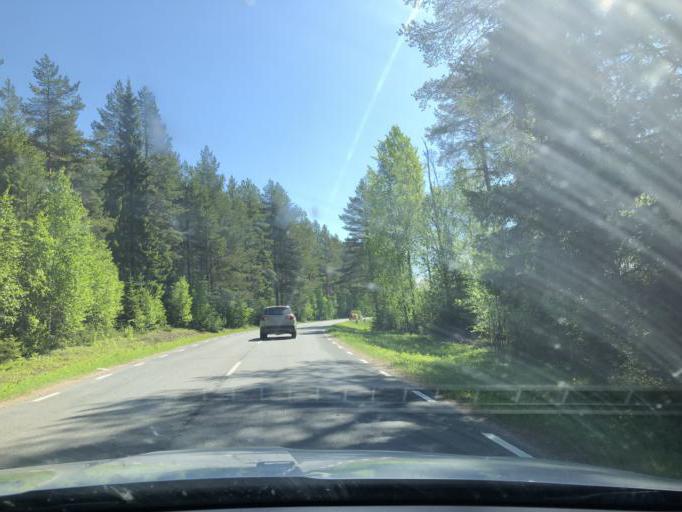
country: SE
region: Norrbotten
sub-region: Lulea Kommun
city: Gammelstad
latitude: 65.6556
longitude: 22.0113
